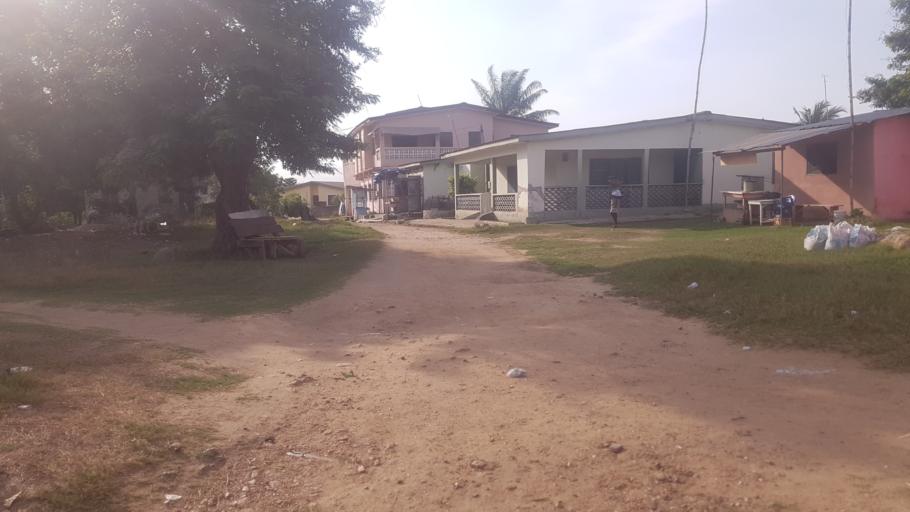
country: GH
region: Central
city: Winneba
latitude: 5.3543
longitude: -0.6297
